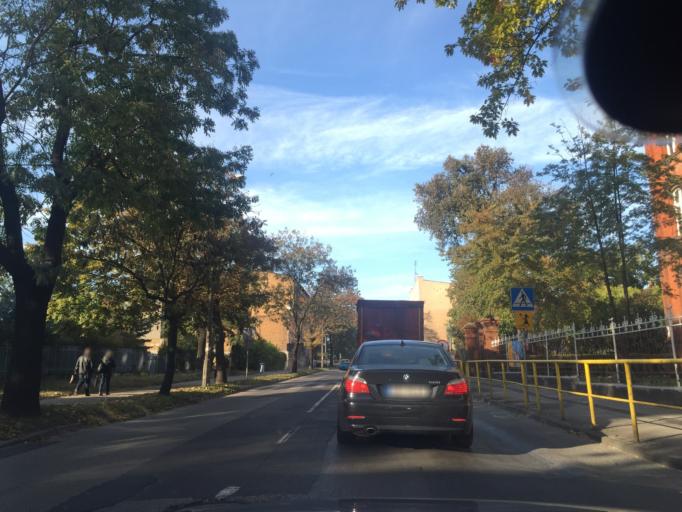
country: PL
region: Kujawsko-Pomorskie
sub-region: Powiat inowroclawski
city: Inowroclaw
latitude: 52.7985
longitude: 18.2644
